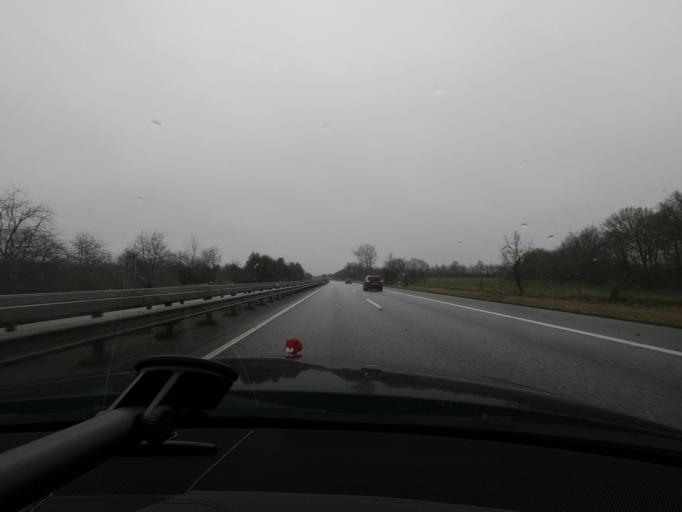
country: DE
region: Schleswig-Holstein
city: Eisendorf
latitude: 54.2084
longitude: 9.8686
